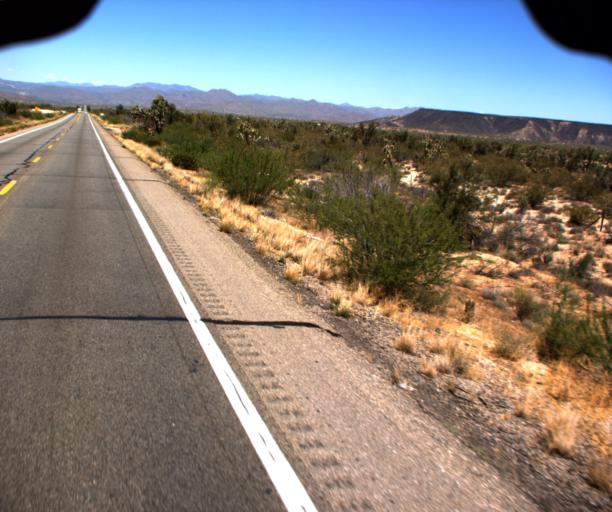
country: US
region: Arizona
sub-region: Yavapai County
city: Congress
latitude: 34.2919
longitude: -113.1115
